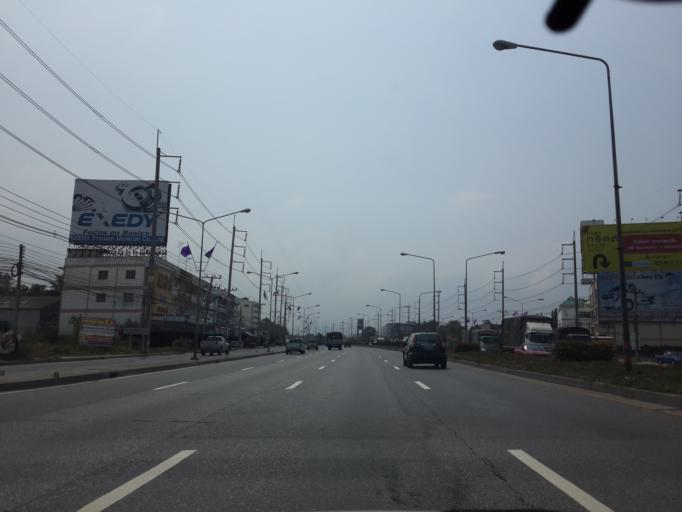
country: TH
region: Chon Buri
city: Chon Buri
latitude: 13.4075
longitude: 101.0014
